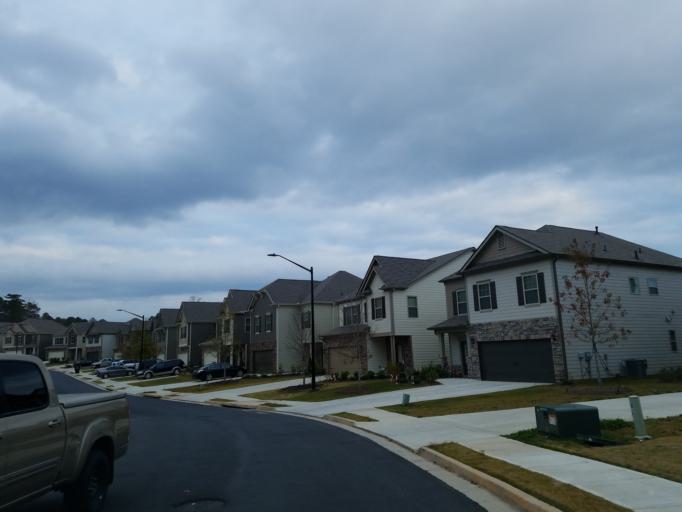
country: US
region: Georgia
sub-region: Cobb County
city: Acworth
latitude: 34.0932
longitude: -84.6282
